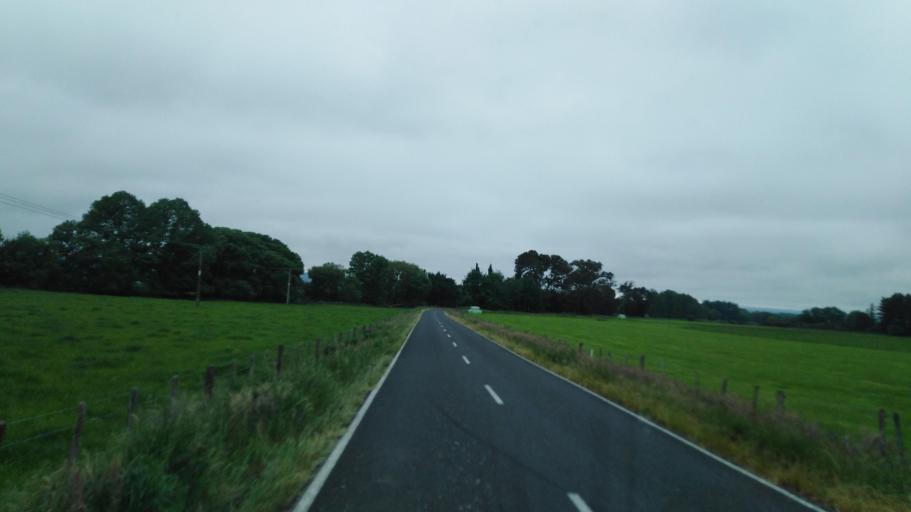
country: NZ
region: Bay of Plenty
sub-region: Rotorua District
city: Rotorua
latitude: -38.4069
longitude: 176.3327
